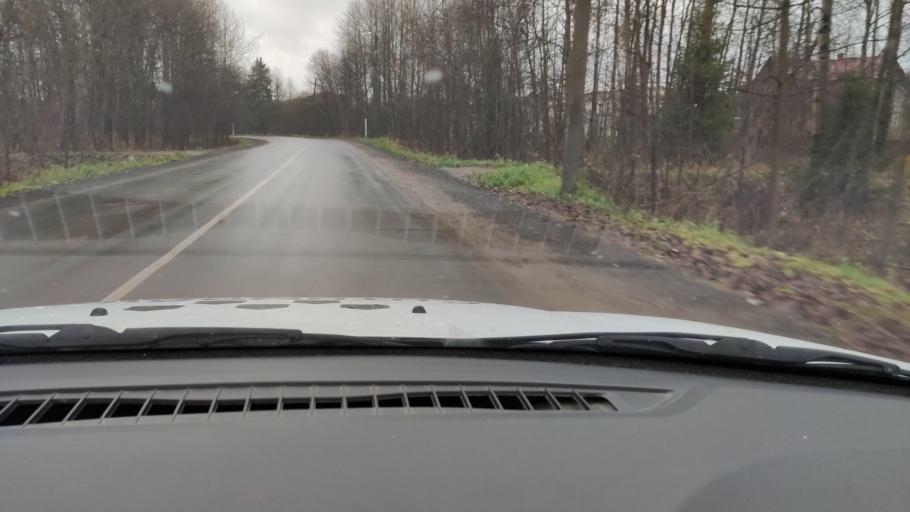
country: RU
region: Perm
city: Sylva
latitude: 58.0346
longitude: 56.7394
